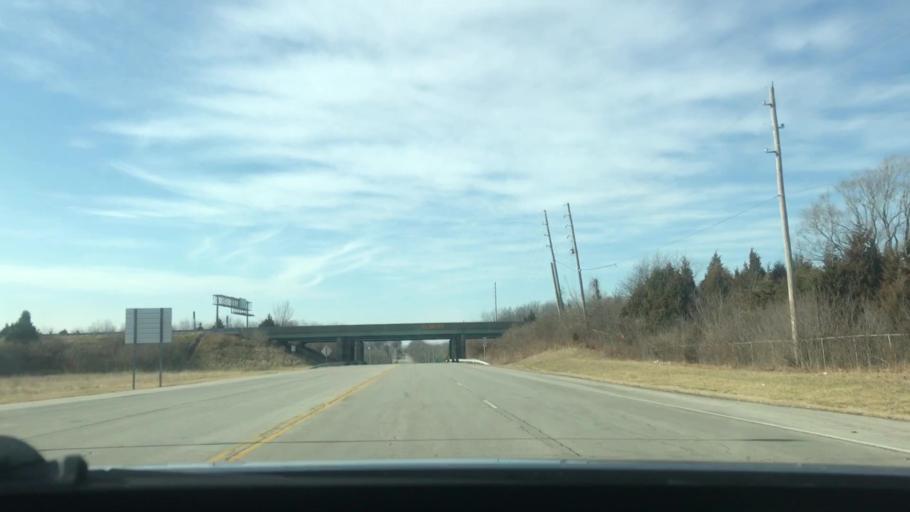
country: US
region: Missouri
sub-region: Clay County
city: Smithville
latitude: 39.3038
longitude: -94.5827
